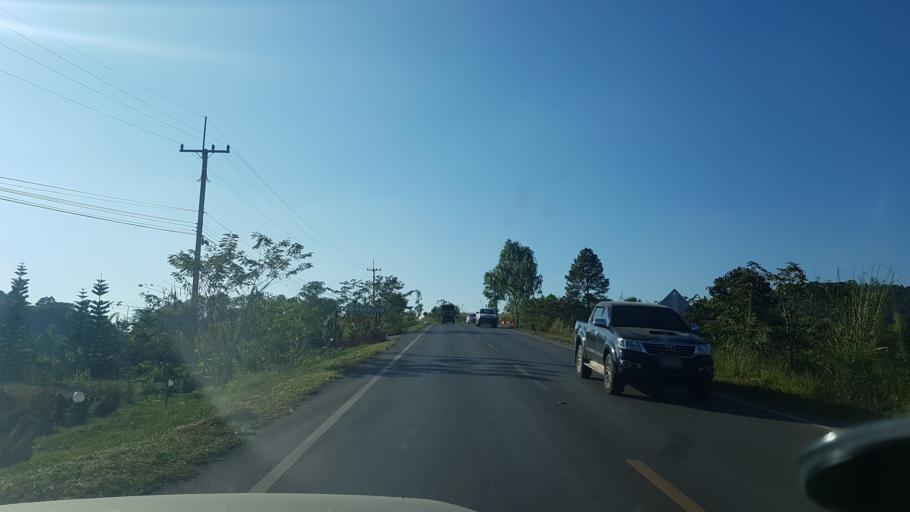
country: TH
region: Phetchabun
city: Khao Kho
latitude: 16.6476
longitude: 101.0047
